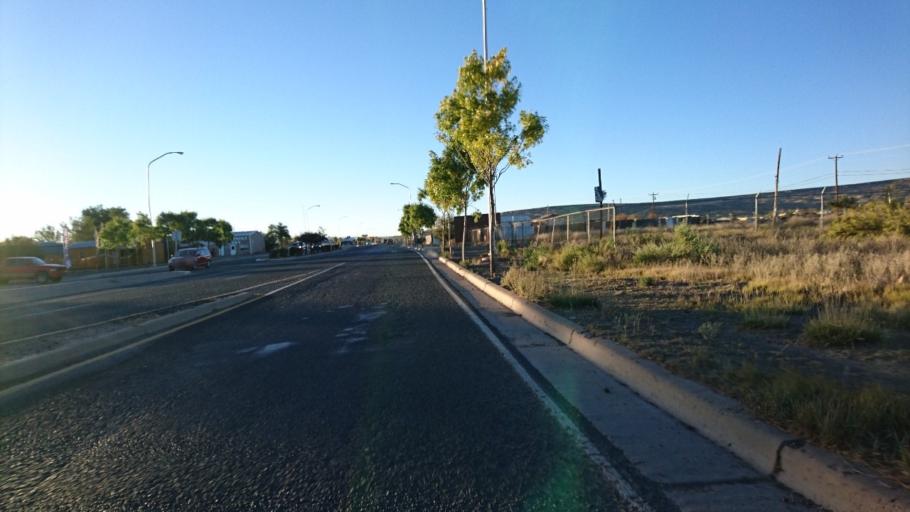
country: US
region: New Mexico
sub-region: Cibola County
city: Grants
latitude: 35.1402
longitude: -107.8292
